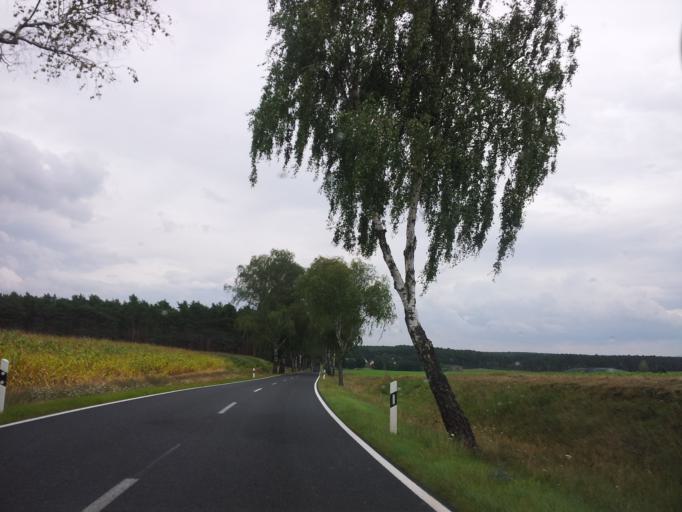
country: DE
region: Brandenburg
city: Gorzke
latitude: 52.1731
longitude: 12.3981
